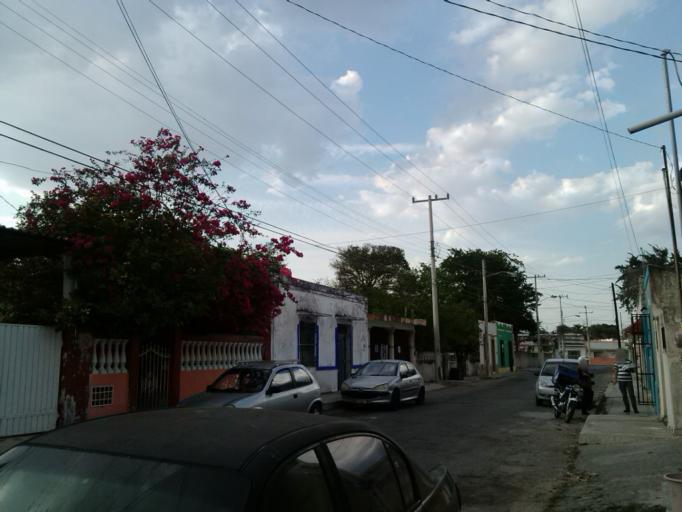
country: MX
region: Yucatan
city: Merida
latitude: 20.9641
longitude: -89.6093
